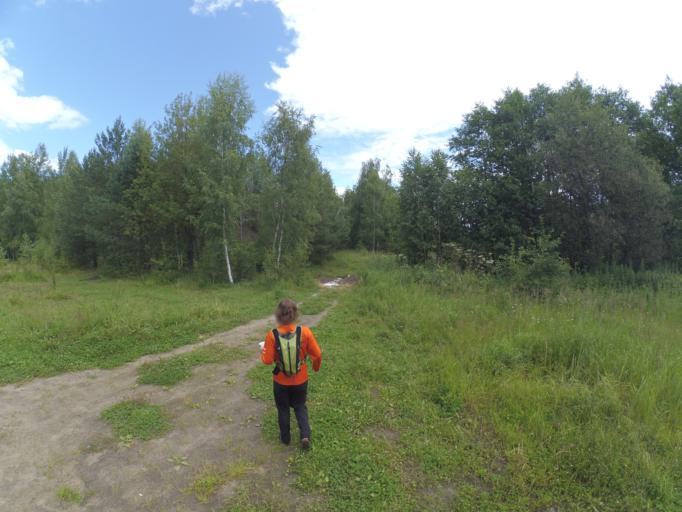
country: RU
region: Moskovskaya
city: Fosforitnyy
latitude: 55.3340
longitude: 38.9124
